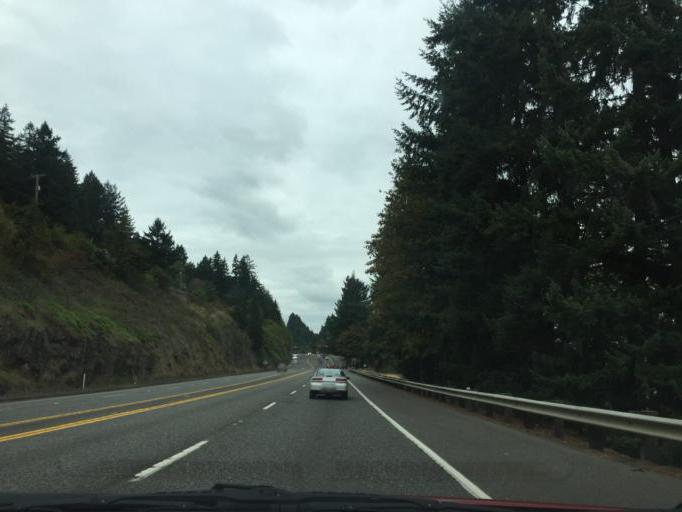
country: US
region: Oregon
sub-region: Washington County
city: Bethany
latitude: 45.6240
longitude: -122.8147
